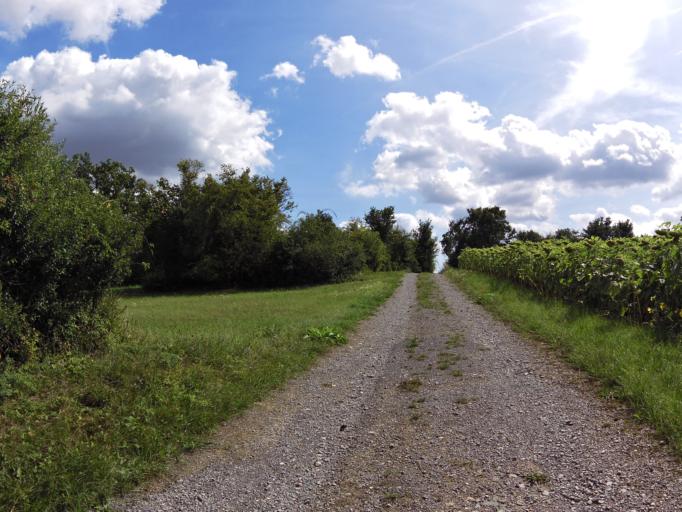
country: DE
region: Bavaria
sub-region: Regierungsbezirk Unterfranken
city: Margetshochheim
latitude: 49.8417
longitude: 9.8473
